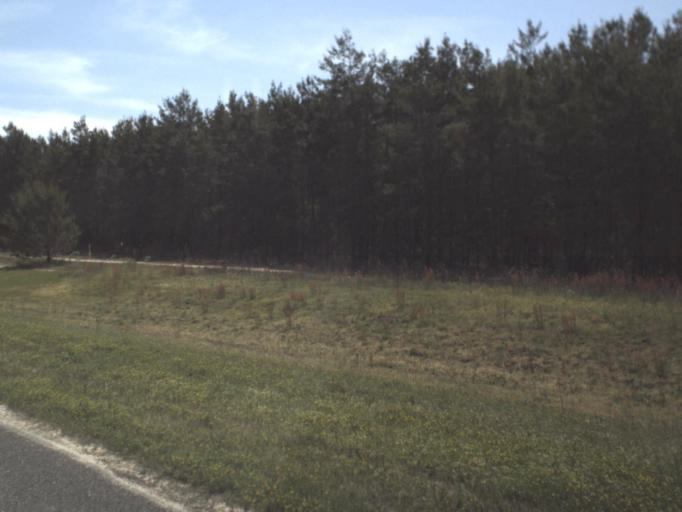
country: US
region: Florida
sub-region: Bay County
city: Lynn Haven
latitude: 30.3992
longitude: -85.6897
